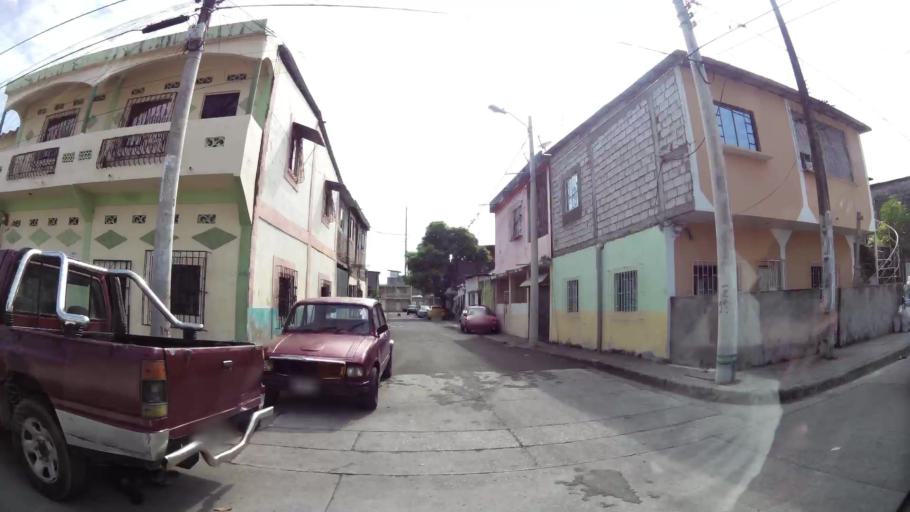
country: EC
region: Guayas
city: Guayaquil
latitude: -2.2563
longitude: -79.8731
